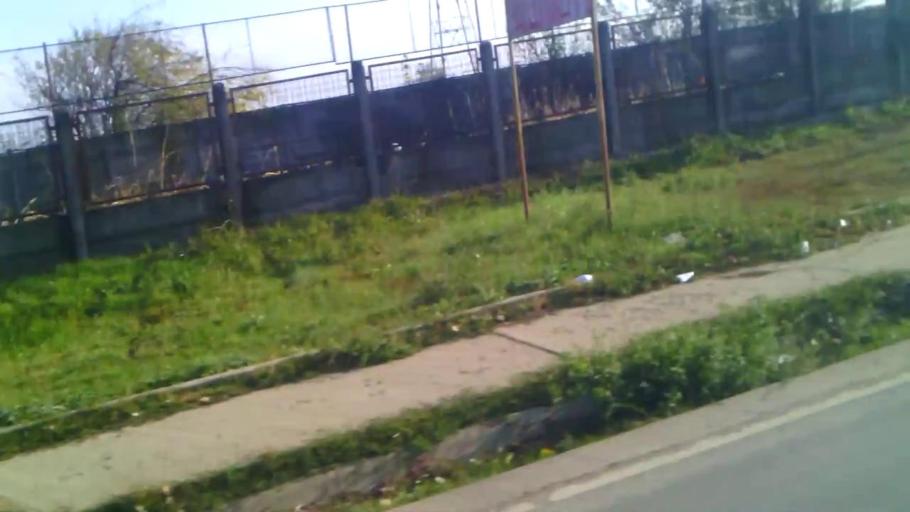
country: RO
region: Ilfov
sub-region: Comuna Popesti-Leordeni
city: Popesti-Leordeni
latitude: 44.3564
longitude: 26.1527
